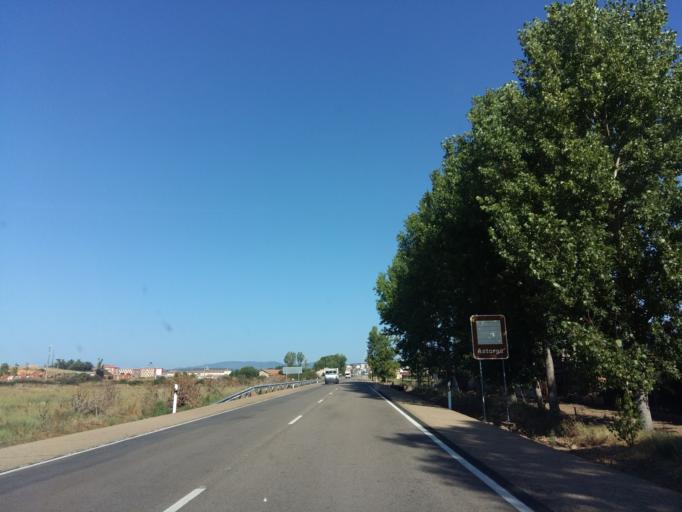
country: ES
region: Castille and Leon
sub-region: Provincia de Leon
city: Astorga
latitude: 42.4441
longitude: -6.0436
